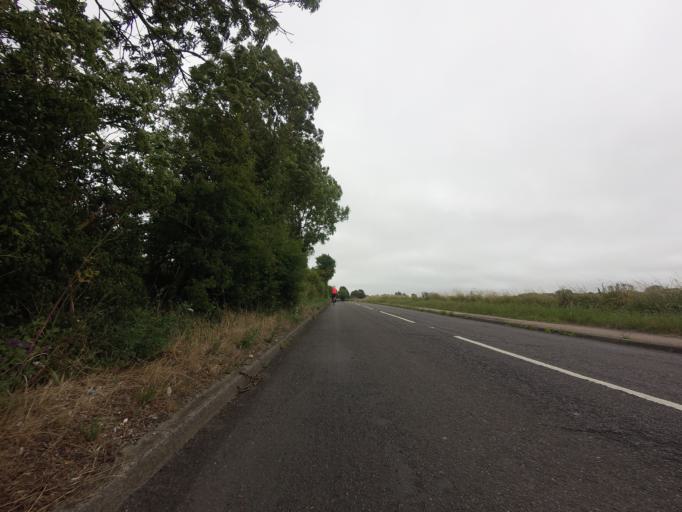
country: GB
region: England
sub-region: Kent
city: Meopham
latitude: 51.3824
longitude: 0.3472
